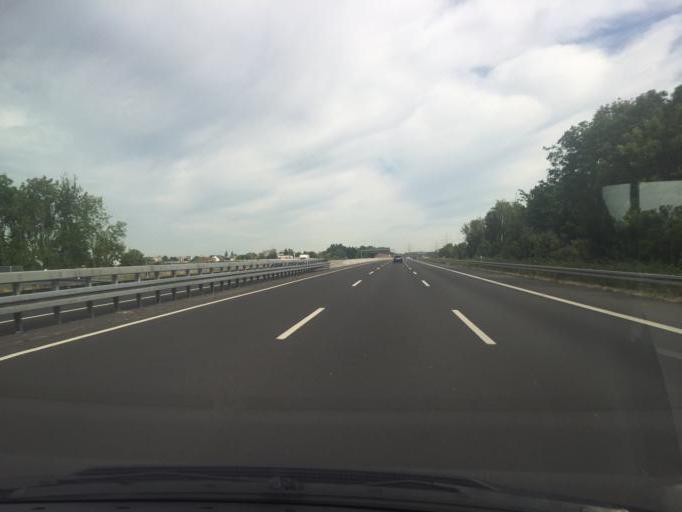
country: DE
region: North Rhine-Westphalia
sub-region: Regierungsbezirk Dusseldorf
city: Dusseldorf
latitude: 51.1547
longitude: 6.7522
